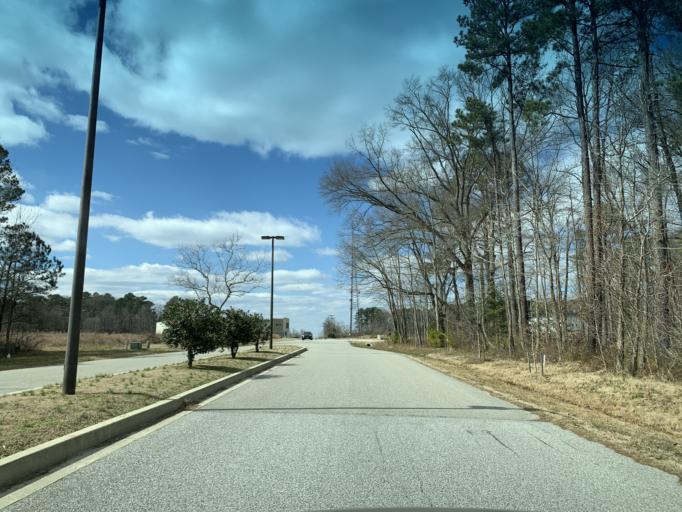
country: US
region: Maryland
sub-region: Queen Anne's County
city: Stevensville
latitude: 38.9537
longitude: -76.3478
